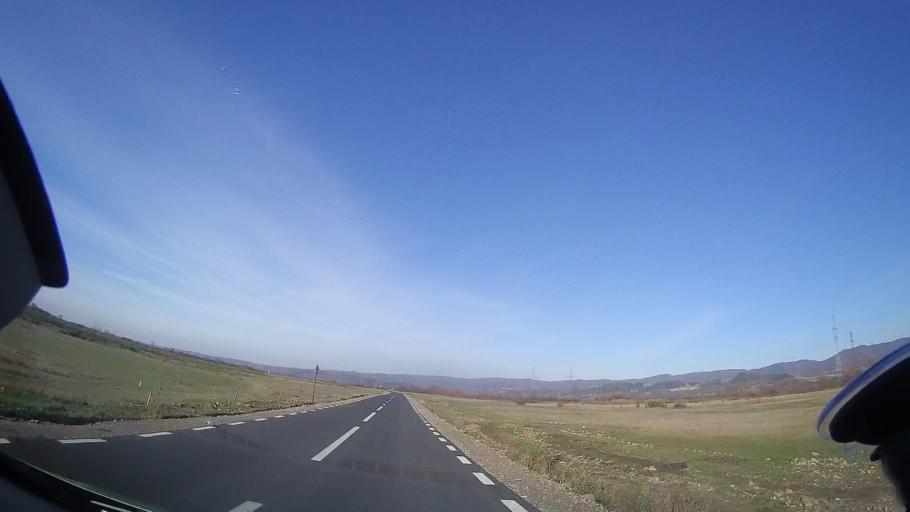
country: RO
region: Bihor
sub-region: Comuna Auseu
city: Auseu
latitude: 47.0088
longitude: 22.5025
